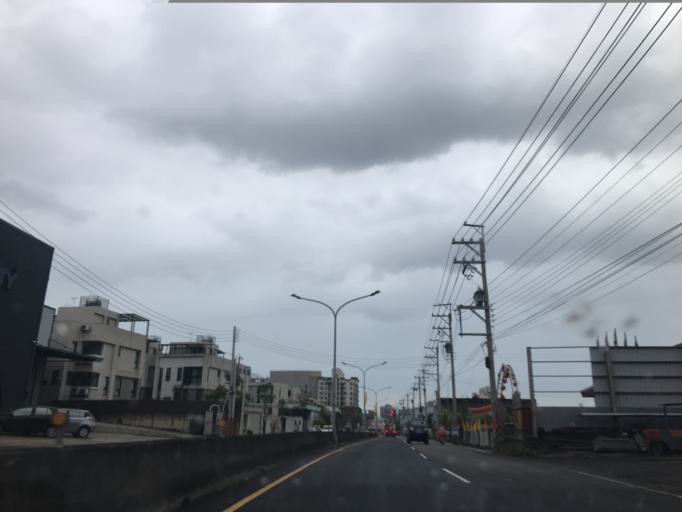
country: TW
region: Taiwan
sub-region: Hsinchu
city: Zhubei
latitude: 24.8314
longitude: 121.0325
